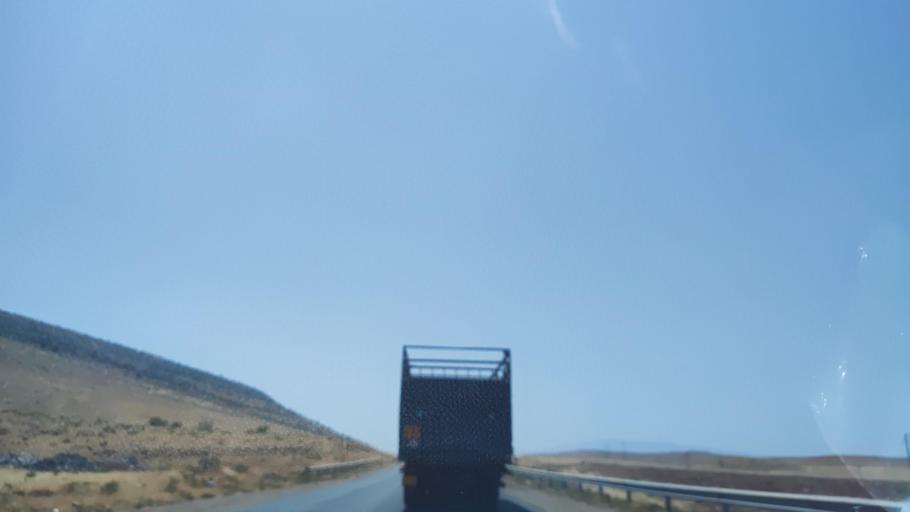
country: IQ
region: Arbil
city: Shaqlawah
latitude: 36.5953
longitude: 44.3181
